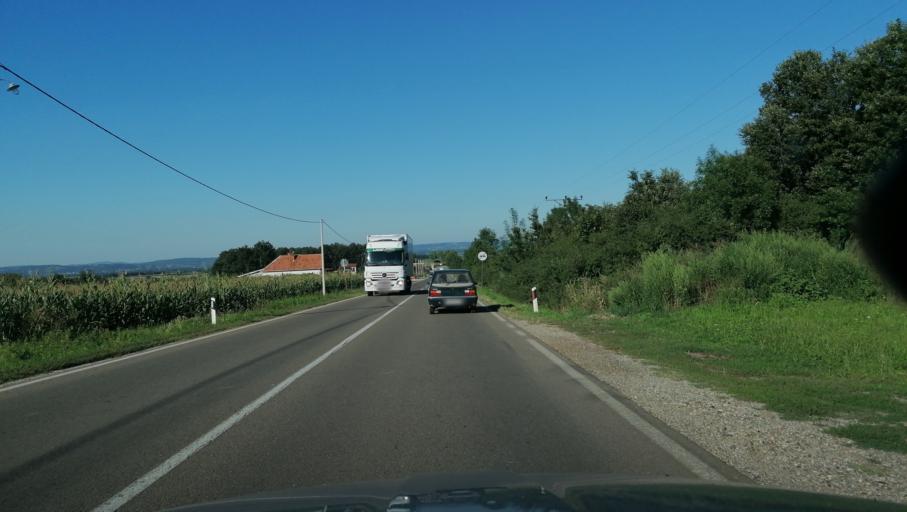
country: RS
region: Central Serbia
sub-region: Sumadijski Okrug
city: Knic
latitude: 43.9099
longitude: 20.6382
